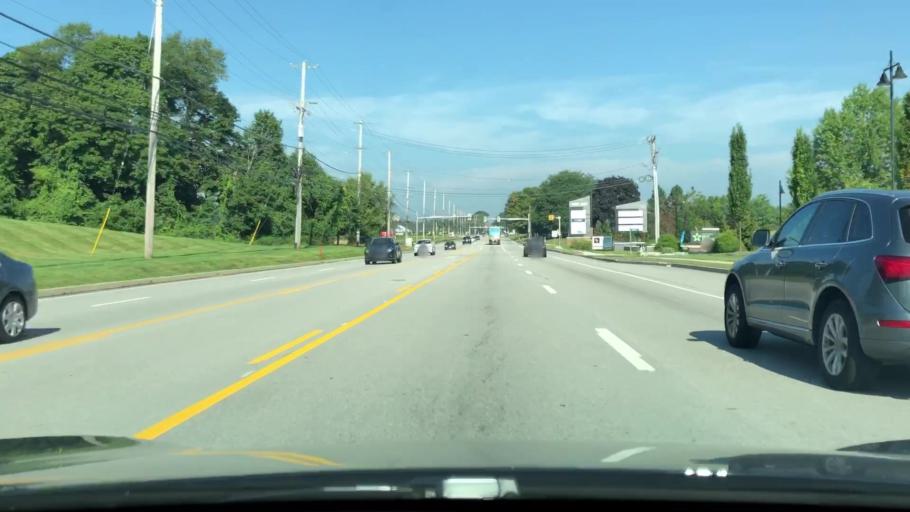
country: US
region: Pennsylvania
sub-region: Montgomery County
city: Horsham
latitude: 40.1580
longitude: -75.1450
